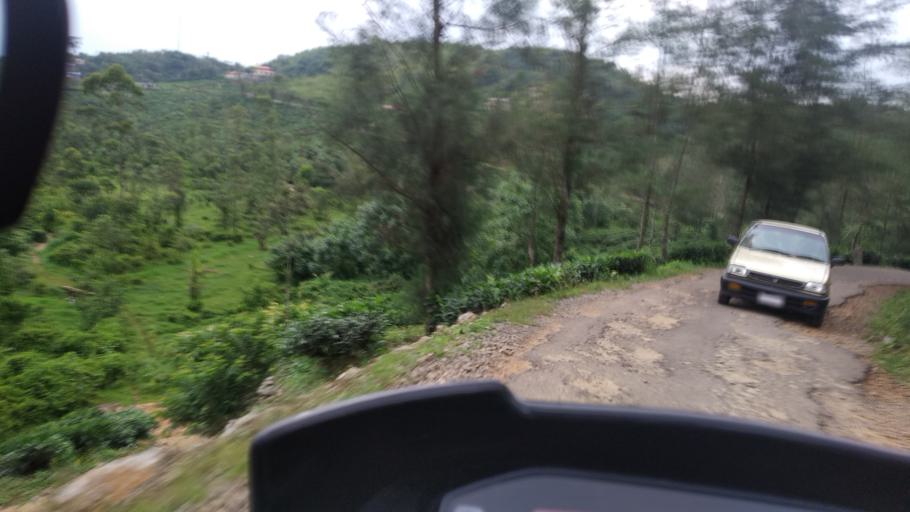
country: IN
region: Tamil Nadu
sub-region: Theni
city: Gudalur
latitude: 9.5423
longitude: 77.0396
